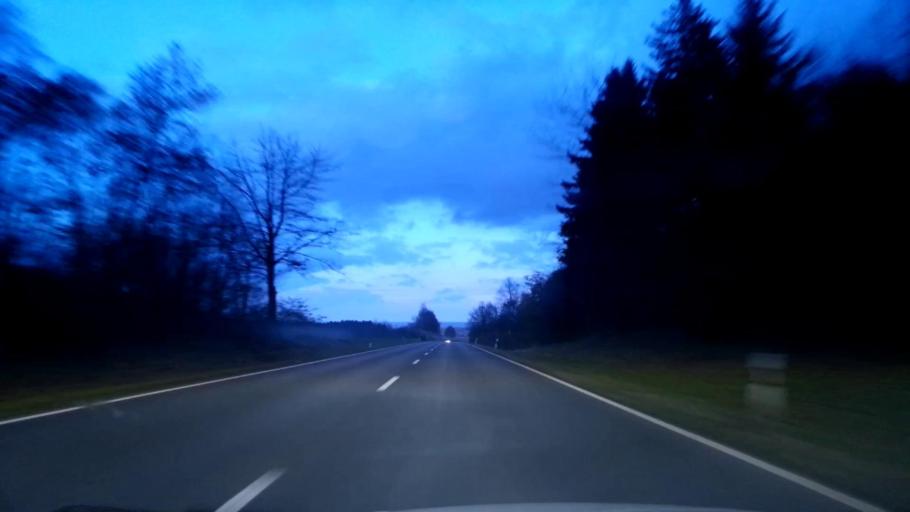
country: DE
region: Bavaria
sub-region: Upper Palatinate
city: Waldershof
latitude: 49.9631
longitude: 12.0933
